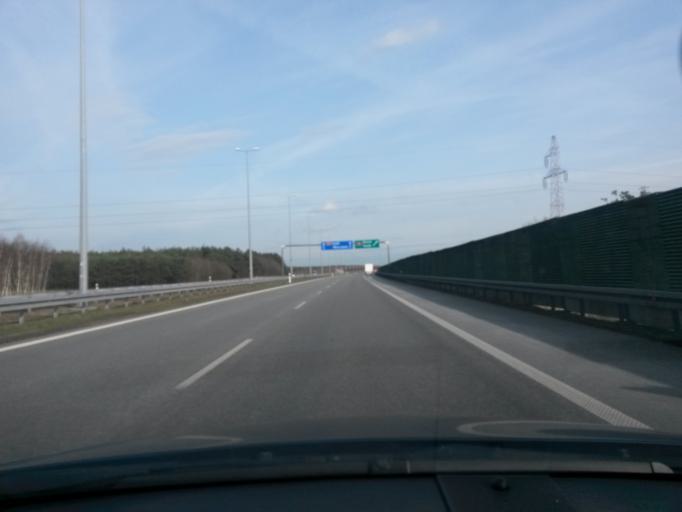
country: PL
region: Greater Poland Voivodeship
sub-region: Powiat koninski
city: Stare Miasto
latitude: 52.1580
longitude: 18.2574
